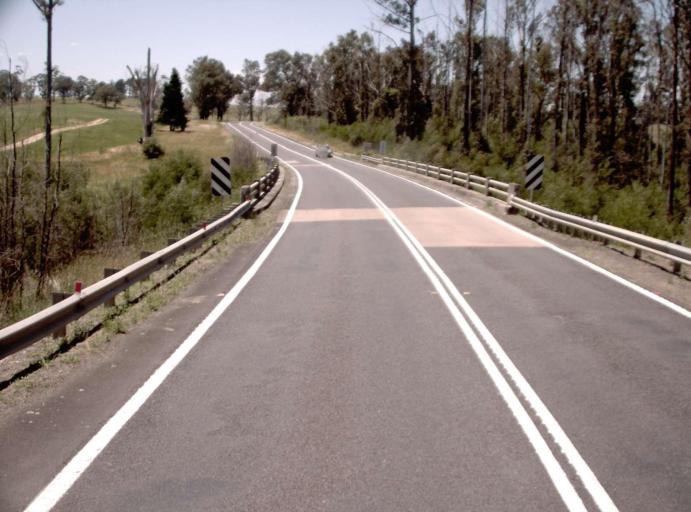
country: AU
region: Victoria
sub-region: East Gippsland
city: Lakes Entrance
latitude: -37.7564
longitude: 148.2755
